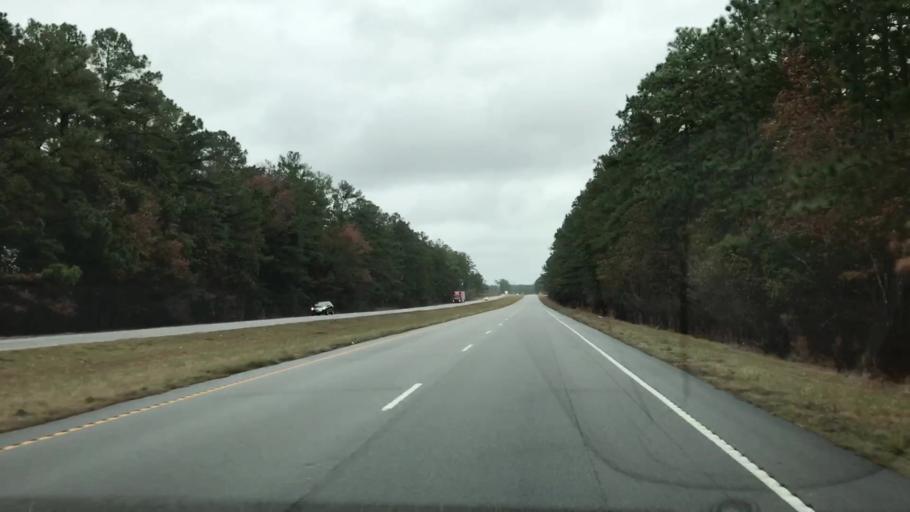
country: US
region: South Carolina
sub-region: Charleston County
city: Awendaw
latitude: 33.1655
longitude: -79.4228
